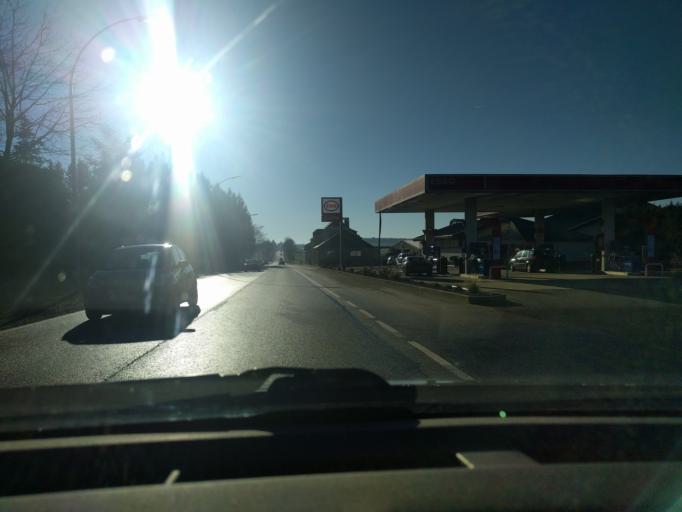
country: LU
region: Diekirch
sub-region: Canton de Clervaux
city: Troisvierges
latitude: 50.1723
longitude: 6.0253
